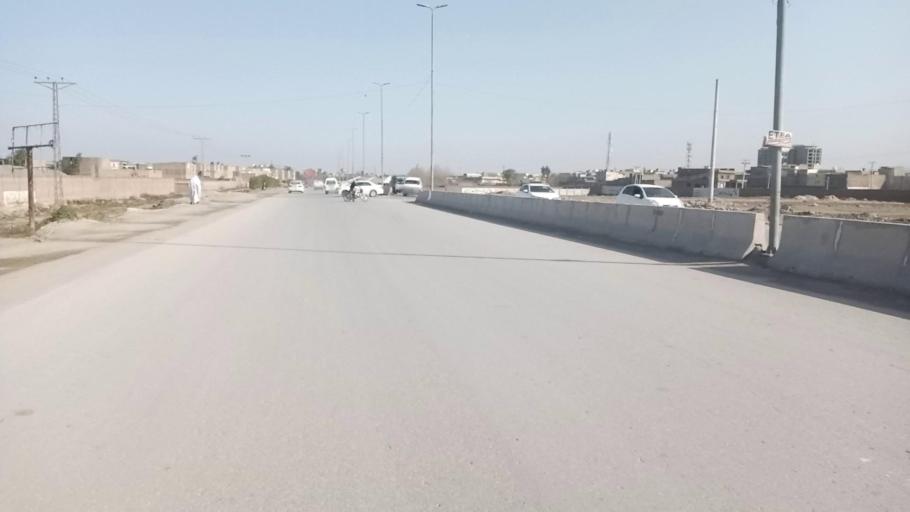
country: PK
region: Khyber Pakhtunkhwa
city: Peshawar
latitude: 34.0336
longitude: 71.5703
